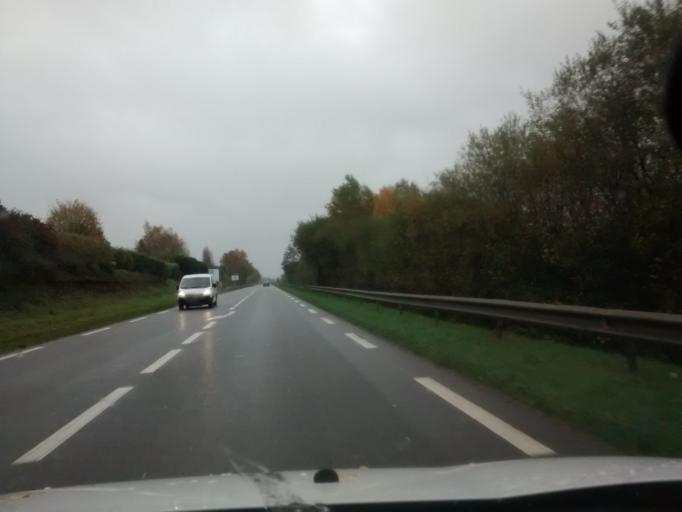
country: FR
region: Brittany
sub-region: Departement d'Ille-et-Vilaine
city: Chantepie
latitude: 48.0811
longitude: -1.6150
